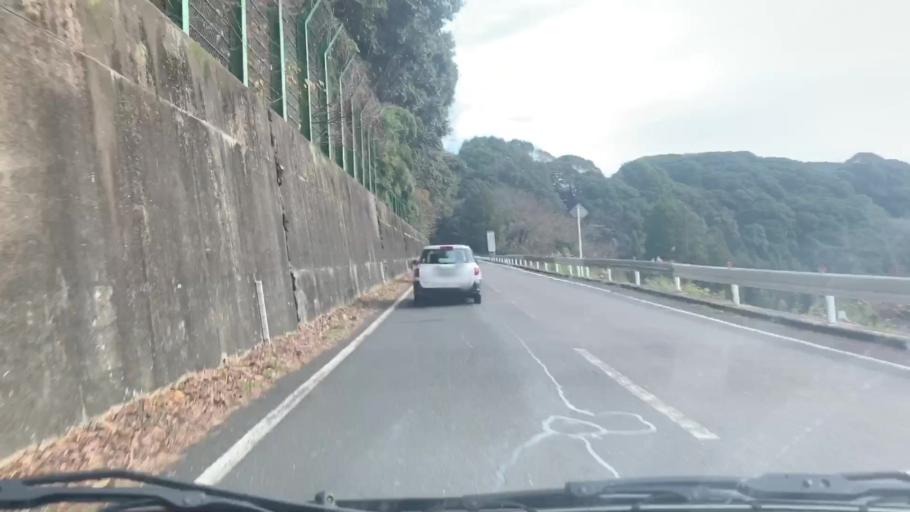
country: JP
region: Saga Prefecture
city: Imaricho-ko
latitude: 33.3285
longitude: 129.9684
